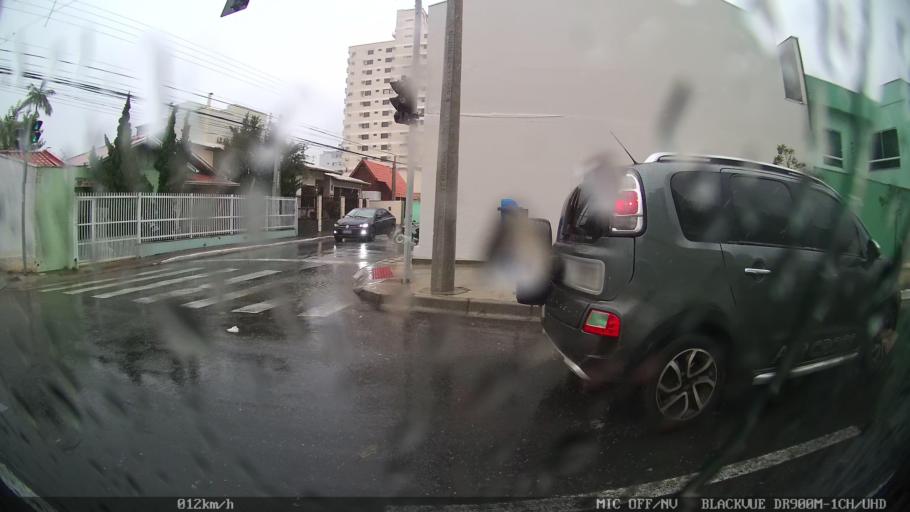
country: BR
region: Santa Catarina
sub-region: Itajai
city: Itajai
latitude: -26.9081
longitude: -48.6662
